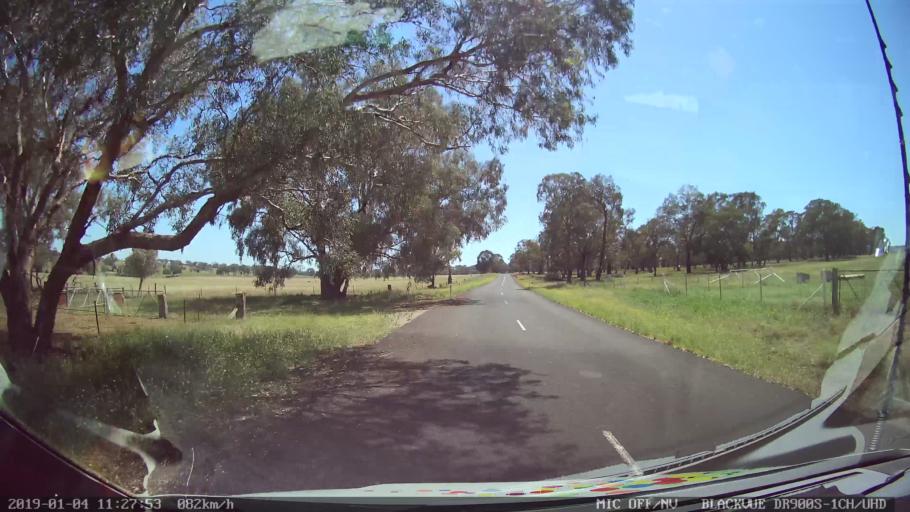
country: AU
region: New South Wales
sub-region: Cabonne
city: Molong
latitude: -33.1051
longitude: 148.7669
